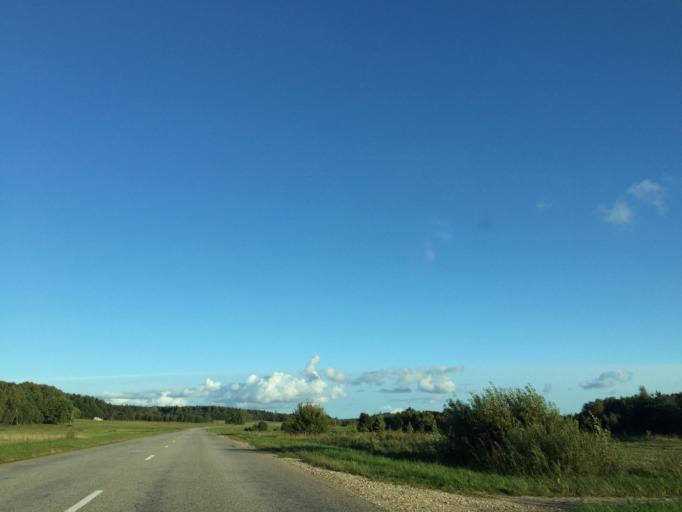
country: LV
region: Kuldigas Rajons
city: Kuldiga
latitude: 56.9304
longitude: 22.0425
